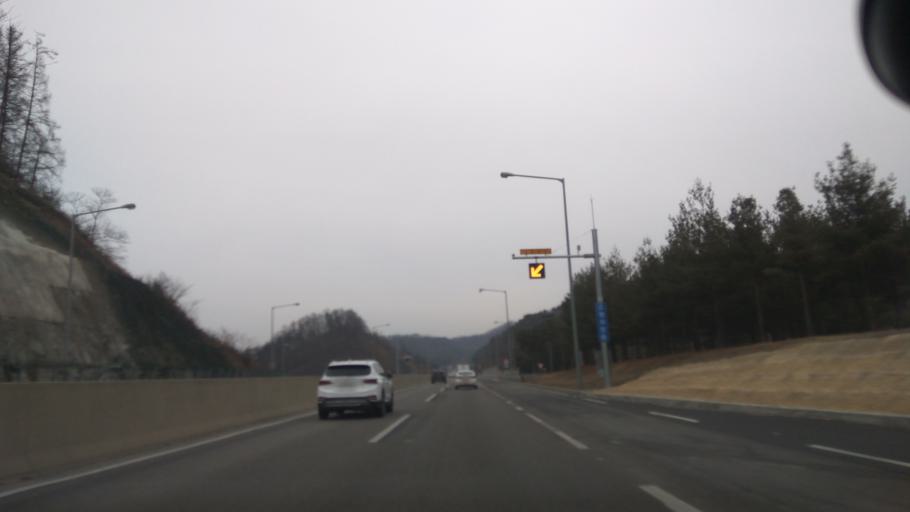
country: KR
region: Gangwon-do
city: Sindong
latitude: 37.7336
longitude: 127.6221
